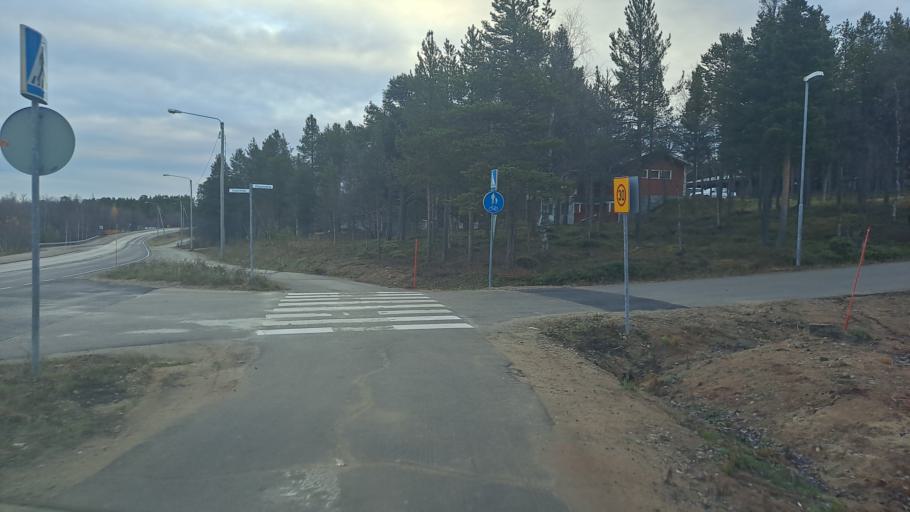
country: FI
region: Lapland
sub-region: Pohjois-Lappi
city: Inari
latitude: 68.9021
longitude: 27.0358
